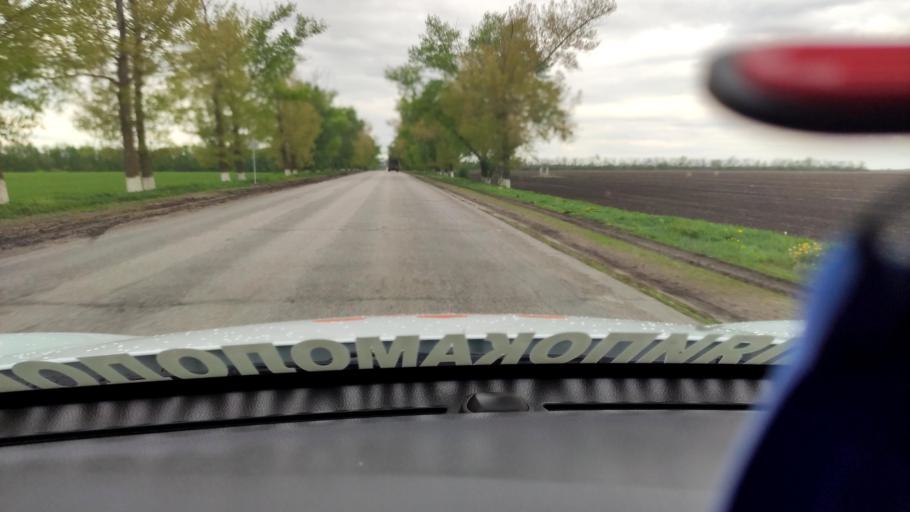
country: RU
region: Voronezj
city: Liski
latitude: 51.0279
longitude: 39.6025
